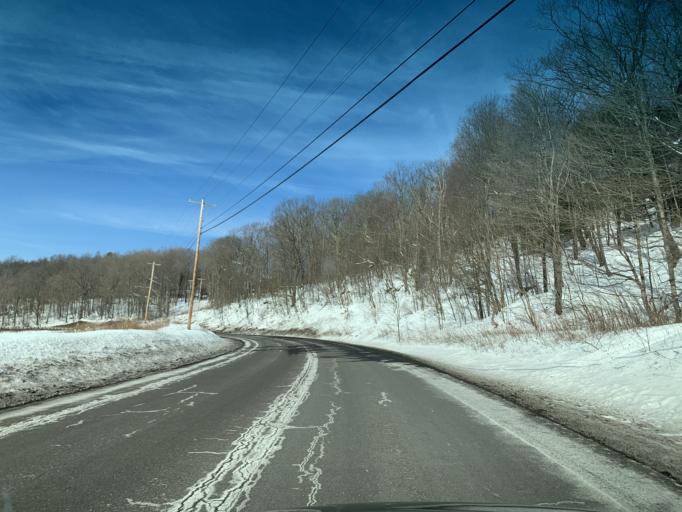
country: US
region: Maryland
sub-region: Allegany County
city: Lonaconing
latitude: 39.5945
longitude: -78.9435
